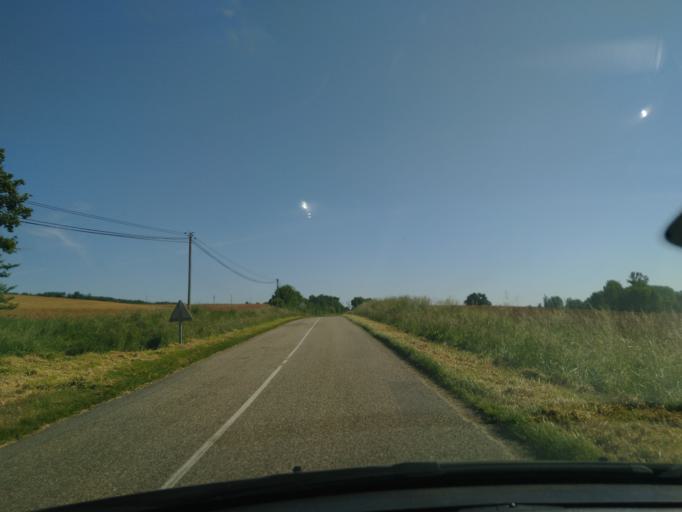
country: FR
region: Midi-Pyrenees
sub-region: Departement du Gers
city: Aubiet
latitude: 43.5680
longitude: 0.8081
